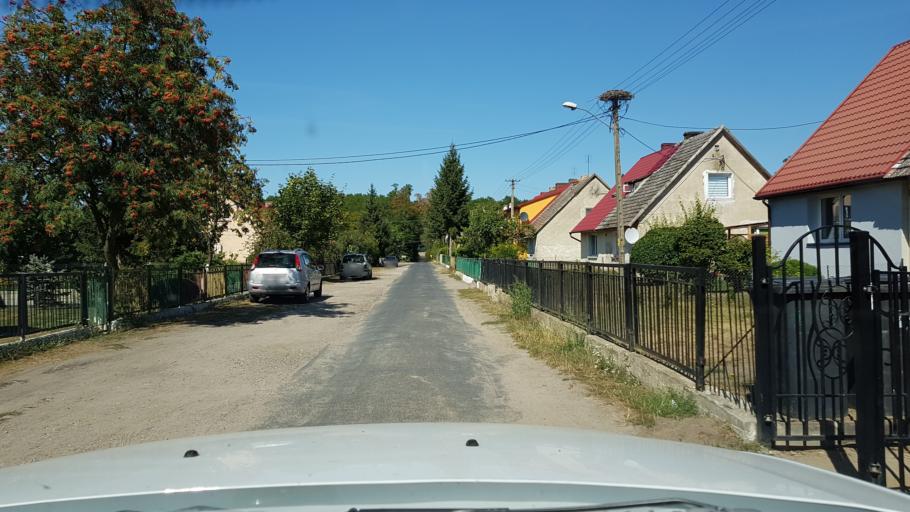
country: PL
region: West Pomeranian Voivodeship
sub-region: Powiat gryfinski
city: Cedynia
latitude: 52.8664
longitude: 14.2307
